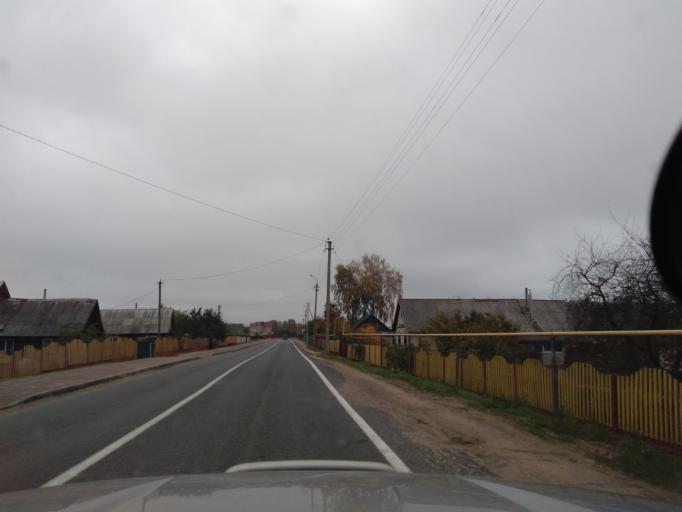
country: BY
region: Minsk
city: Kapyl'
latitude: 53.1433
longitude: 27.0920
